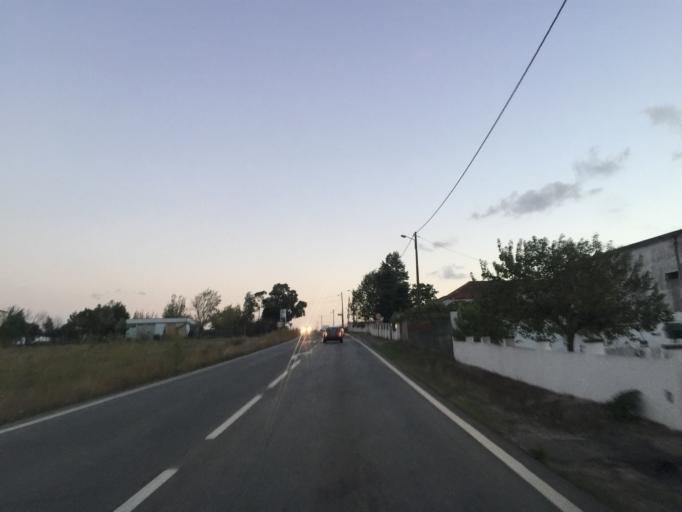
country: PT
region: Lisbon
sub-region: Alenquer
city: Alenquer
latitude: 39.1343
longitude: -8.9973
